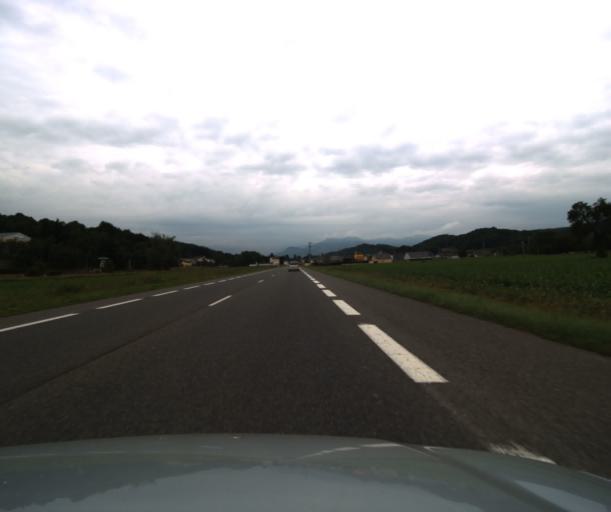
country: FR
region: Midi-Pyrenees
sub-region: Departement des Hautes-Pyrenees
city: Ossun
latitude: 43.1460
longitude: -0.0248
